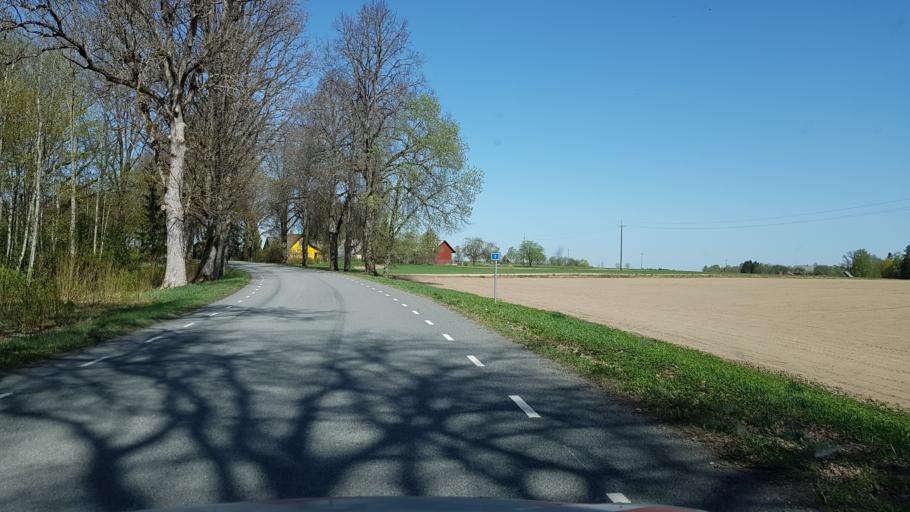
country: EE
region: Viljandimaa
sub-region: Vohma linn
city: Vohma
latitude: 58.5363
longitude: 25.5826
